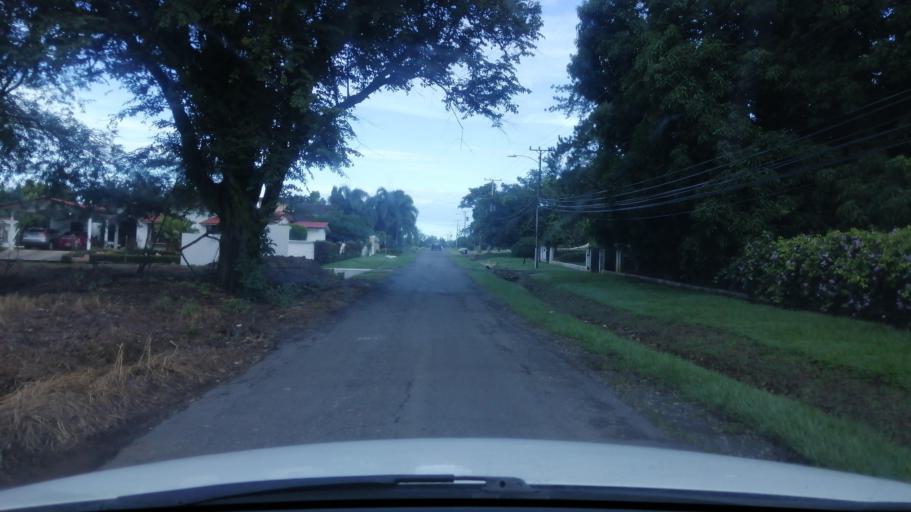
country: PA
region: Chiriqui
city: Mata del Nance
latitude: 8.4579
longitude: -82.4145
